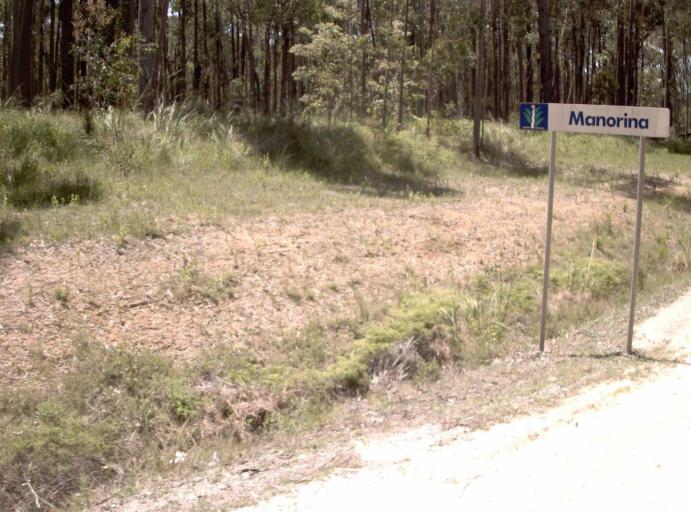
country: AU
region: Victoria
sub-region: East Gippsland
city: Lakes Entrance
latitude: -37.6740
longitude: 148.7917
